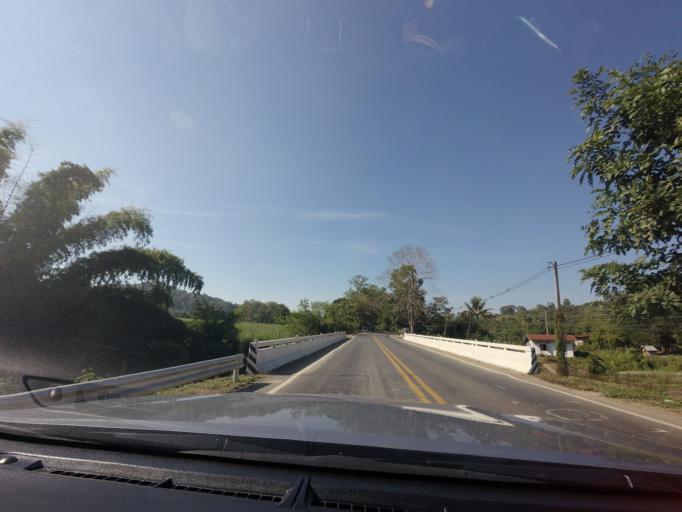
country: TH
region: Sukhothai
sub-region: Amphoe Si Satchanalai
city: Si Satchanalai
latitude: 17.6182
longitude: 99.7088
